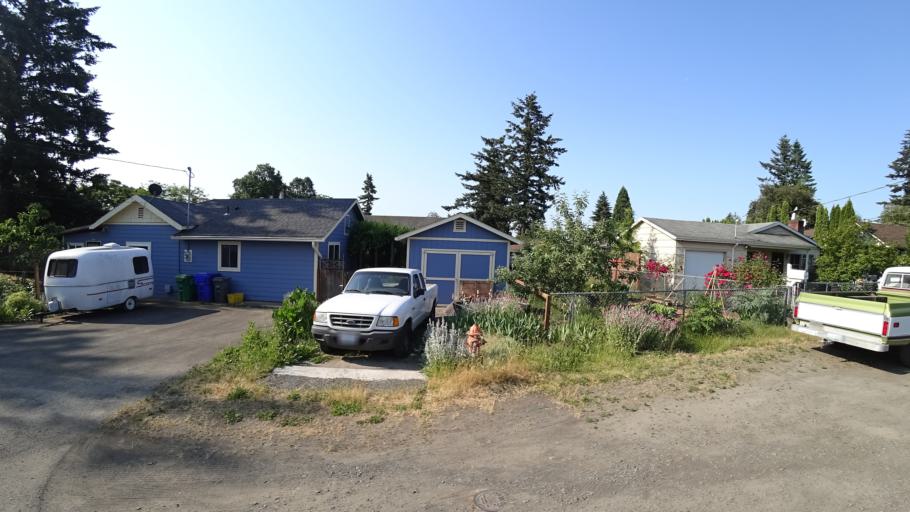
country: US
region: Oregon
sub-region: Multnomah County
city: Lents
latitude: 45.4624
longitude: -122.5872
